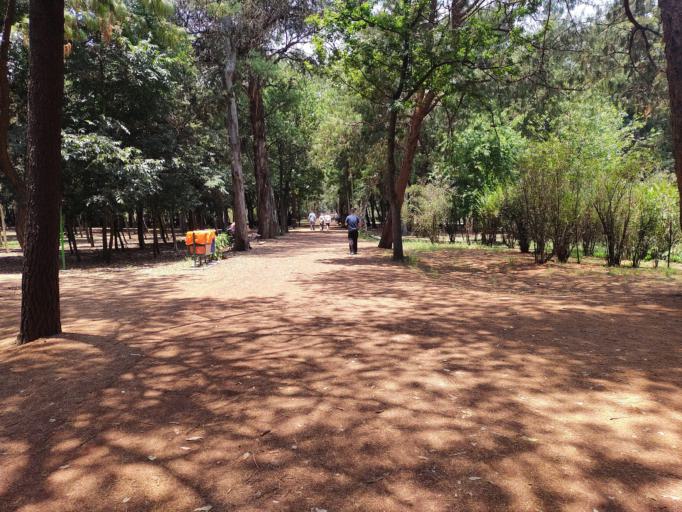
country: MX
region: Mexico City
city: Coyoacan
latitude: 19.3539
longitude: -99.1691
